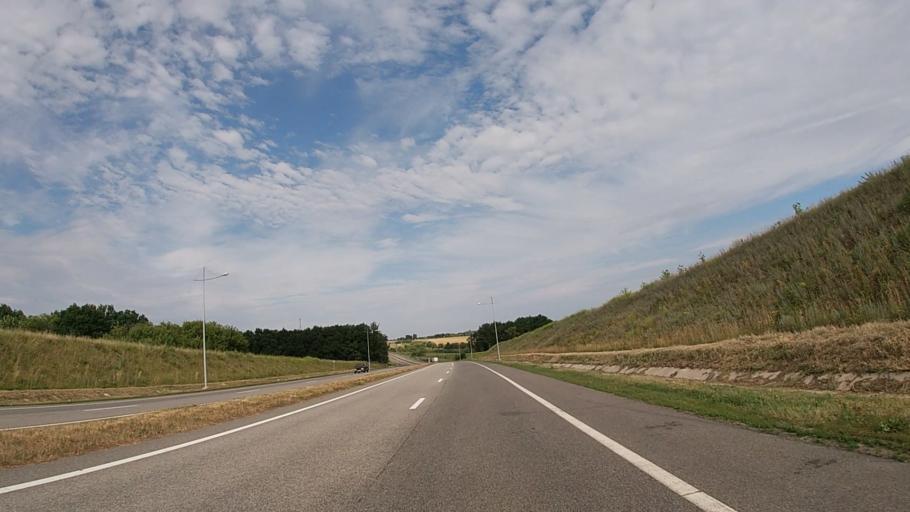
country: RU
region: Belgorod
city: Tomarovka
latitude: 50.7068
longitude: 36.2110
